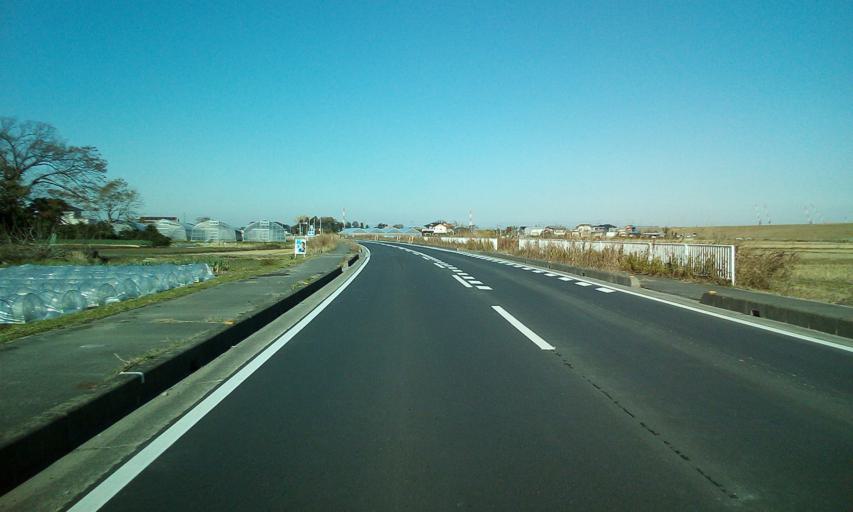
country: JP
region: Chiba
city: Nagareyama
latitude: 35.8836
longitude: 139.8866
